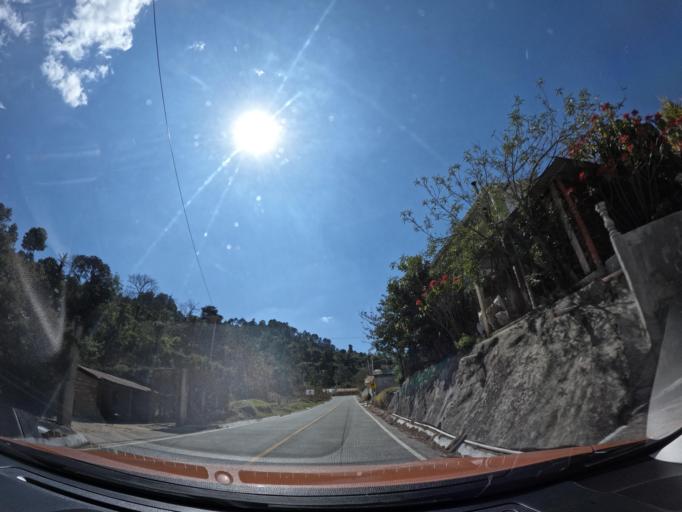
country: GT
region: Solola
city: San Antonio Palopo
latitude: 14.6937
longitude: -91.0720
